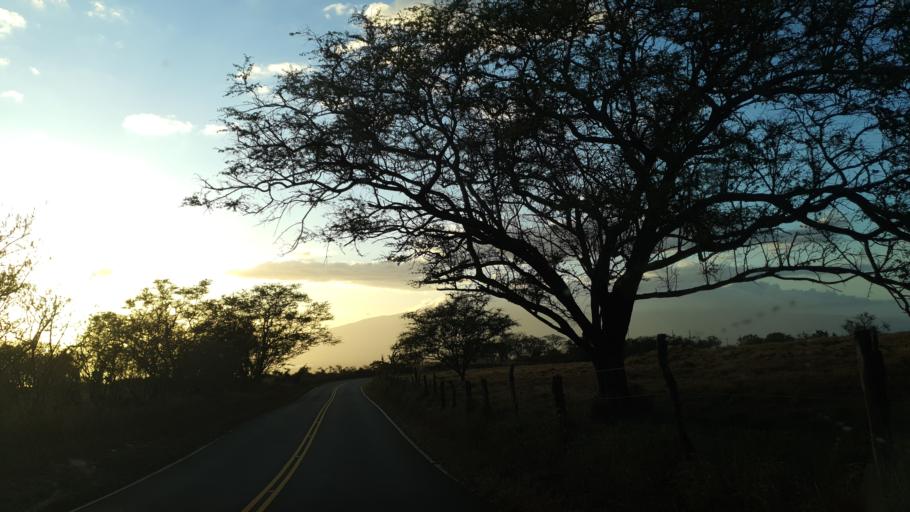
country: US
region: Hawaii
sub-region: Maui County
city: Pukalani
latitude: 20.7840
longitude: -156.3461
